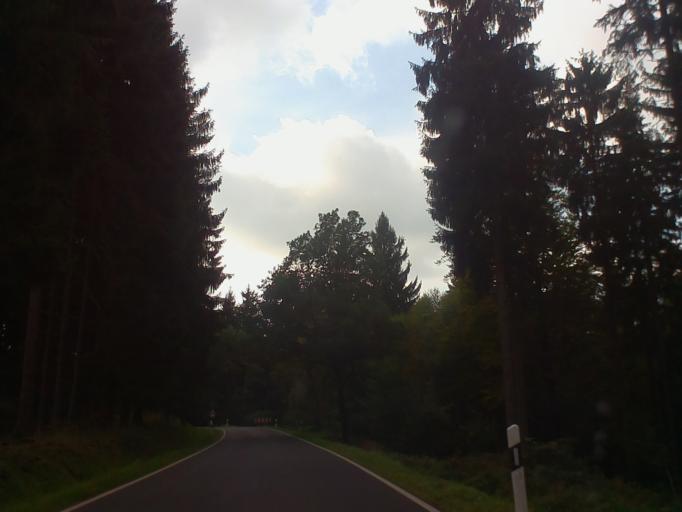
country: DE
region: Thuringia
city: Grossensee
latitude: 50.9258
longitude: 9.9197
